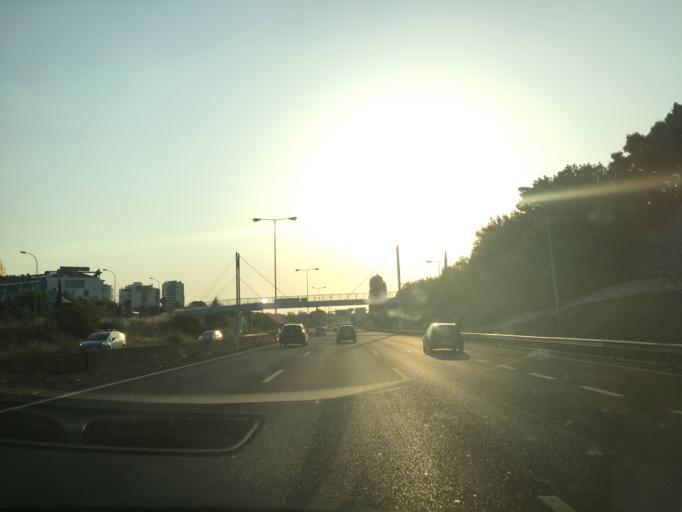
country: PT
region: Lisbon
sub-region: Amadora
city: Amadora
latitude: 38.7403
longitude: -9.2164
